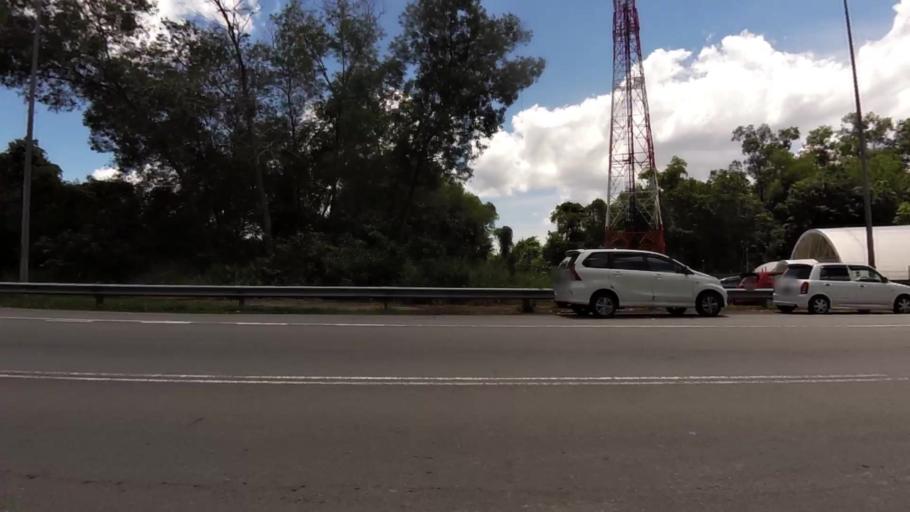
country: BN
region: Brunei and Muara
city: Bandar Seri Begawan
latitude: 4.9280
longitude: 114.9577
